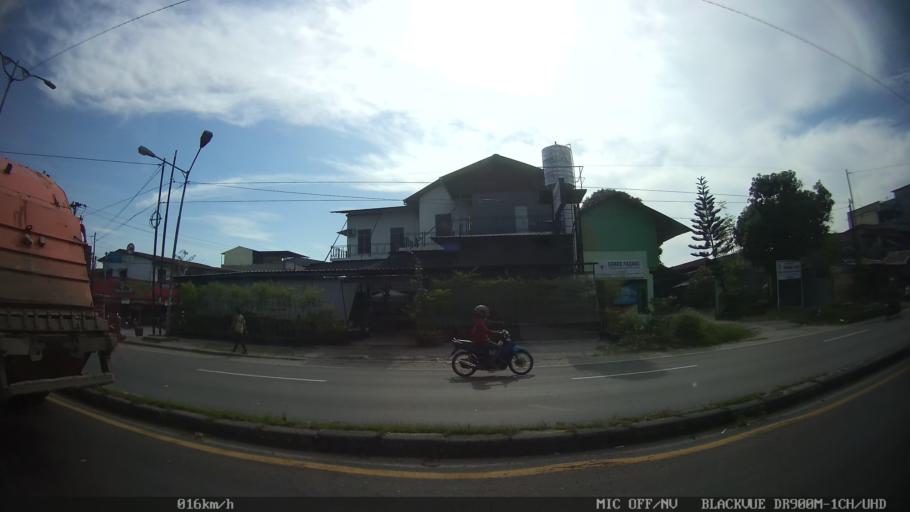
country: ID
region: North Sumatra
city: Sunggal
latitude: 3.6097
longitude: 98.6276
